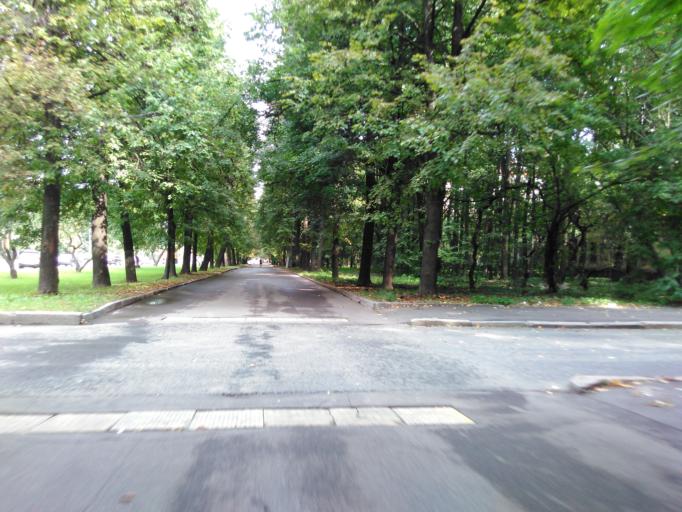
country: RU
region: Moscow
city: Vorob'yovo
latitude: 55.7024
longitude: 37.5239
